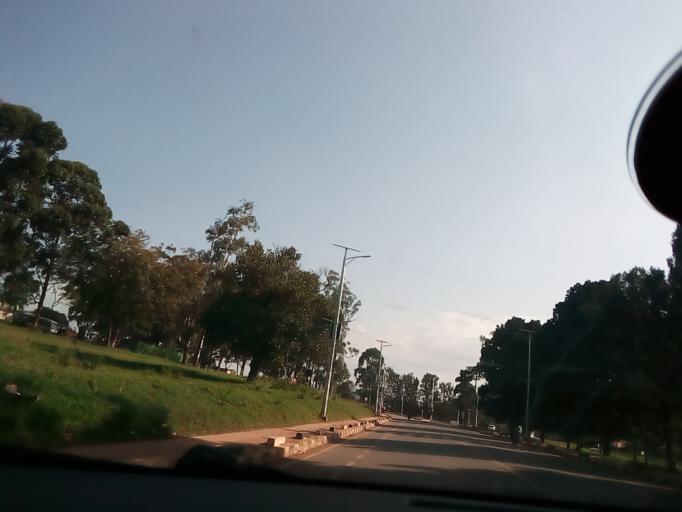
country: UG
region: Central Region
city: Masaka
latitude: -0.3317
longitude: 31.7379
